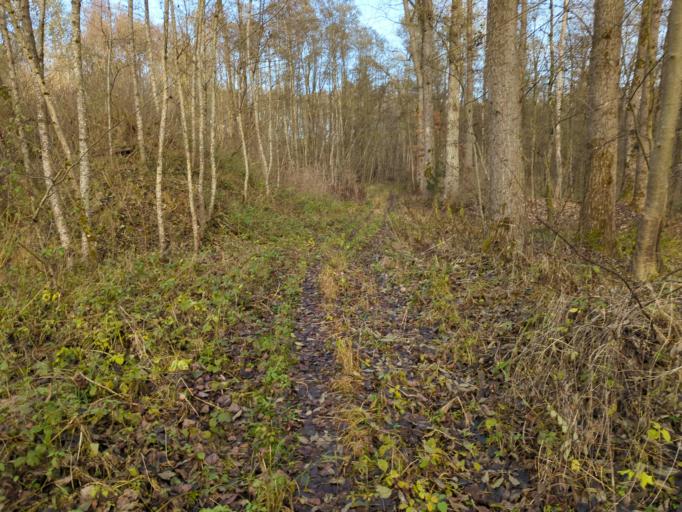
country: DE
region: Bavaria
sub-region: Swabia
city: Wasserburg
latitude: 48.4216
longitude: 10.3033
